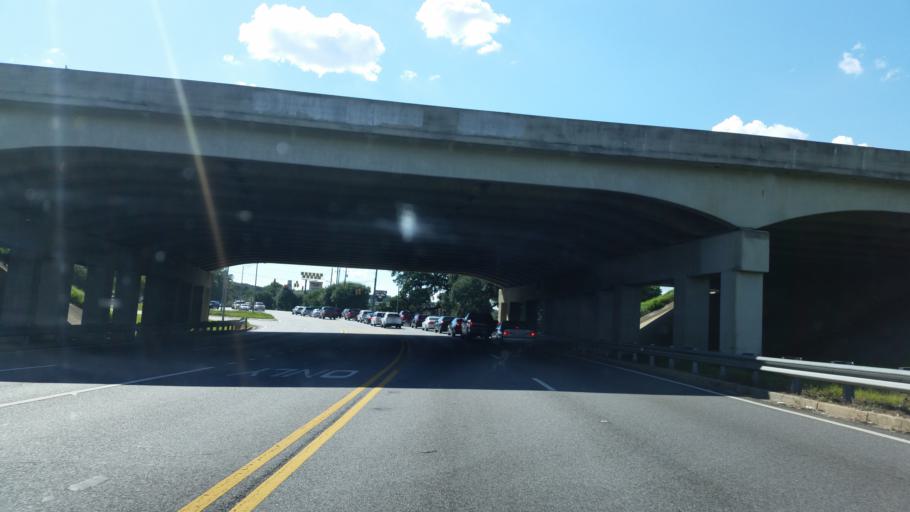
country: US
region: Alabama
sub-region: Mobile County
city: Prichard
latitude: 30.7037
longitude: -88.1227
